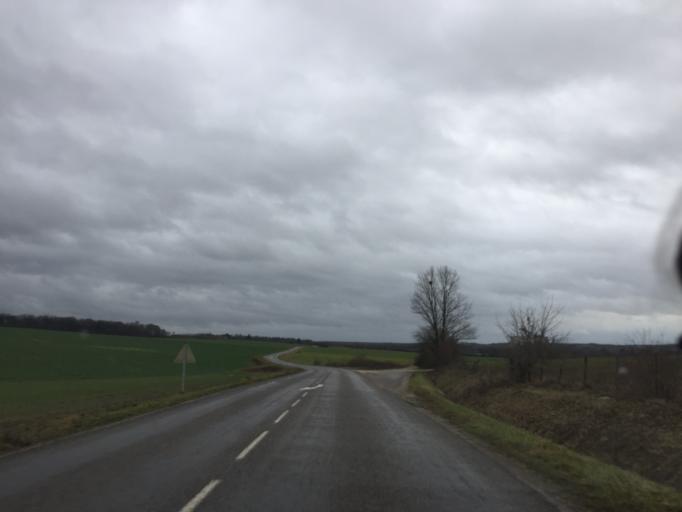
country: FR
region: Franche-Comte
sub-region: Departement du Jura
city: Dole
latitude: 47.1583
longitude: 5.5665
